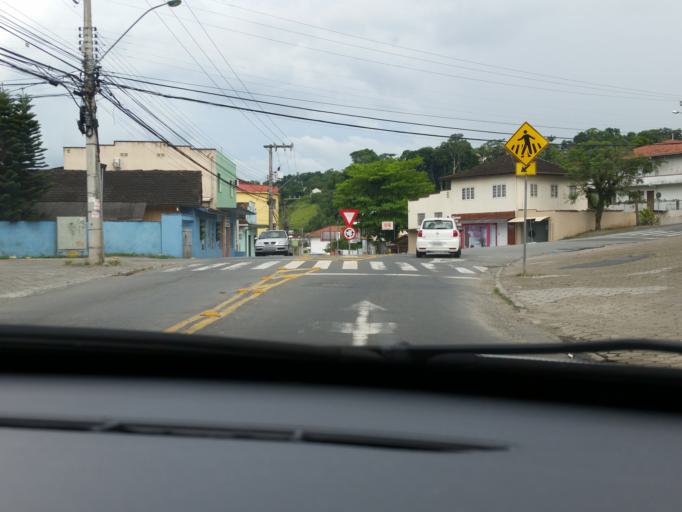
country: BR
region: Santa Catarina
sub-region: Blumenau
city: Blumenau
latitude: -26.9121
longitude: -49.1012
